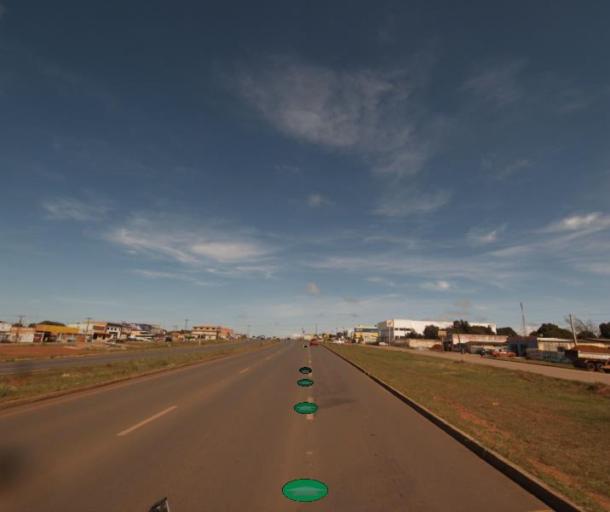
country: BR
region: Federal District
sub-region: Brasilia
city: Brasilia
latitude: -15.7354
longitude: -48.2796
